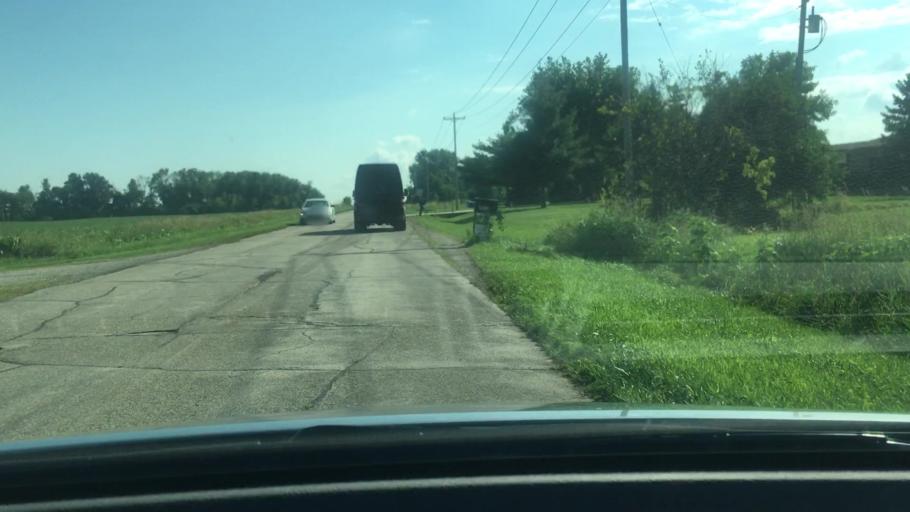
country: US
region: Wisconsin
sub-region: Winnebago County
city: Oshkosh
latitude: 43.9595
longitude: -88.5748
